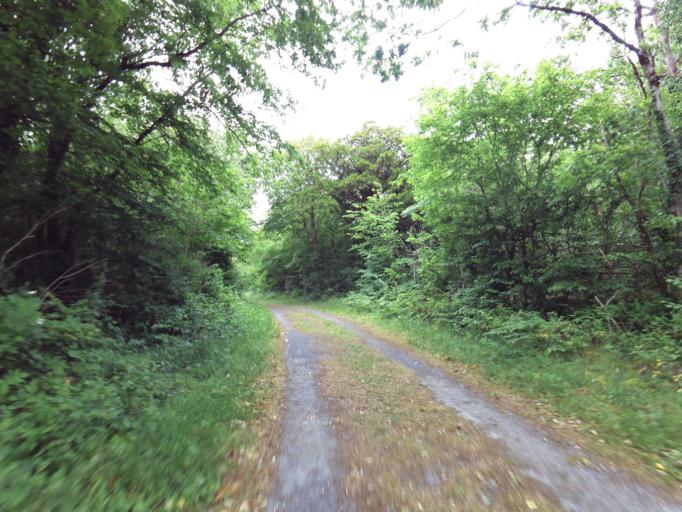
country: IE
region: Connaught
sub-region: County Galway
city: Gort
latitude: 53.0821
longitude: -8.8676
